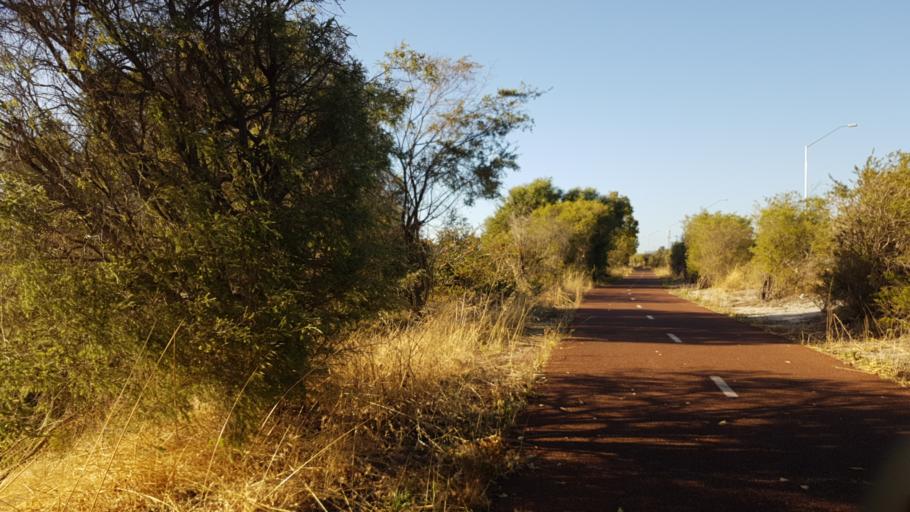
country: AU
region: Western Australia
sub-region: Kwinana
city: Bertram
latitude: -32.2470
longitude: 115.8521
